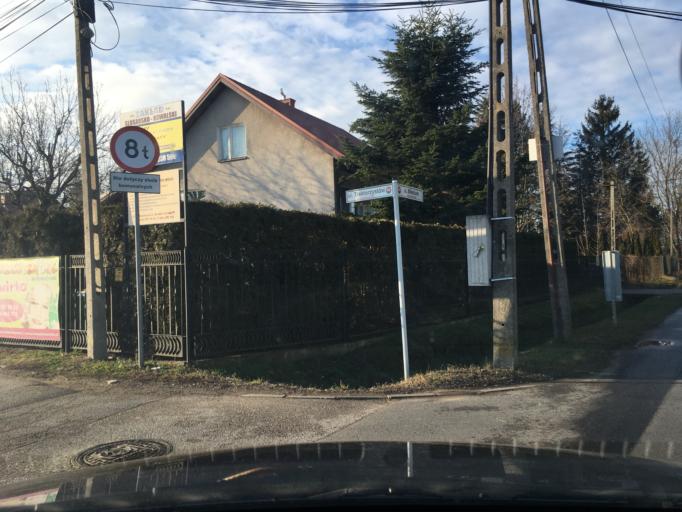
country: PL
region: Masovian Voivodeship
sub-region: Powiat piaseczynski
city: Lesznowola
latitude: 52.0314
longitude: 20.9537
